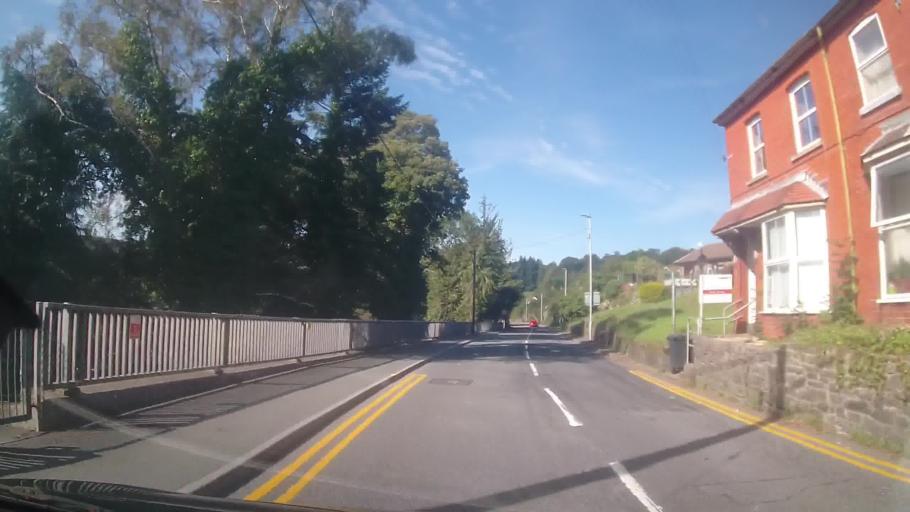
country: GB
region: Wales
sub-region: Sir Powys
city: Rhayader
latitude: 52.3028
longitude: -3.5129
